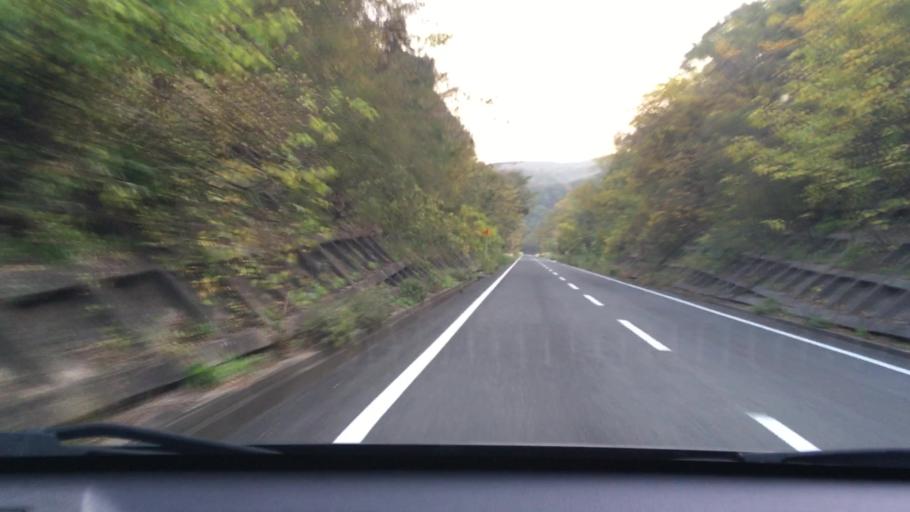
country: JP
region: Nagasaki
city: Sasebo
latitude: 33.0041
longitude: 129.7074
